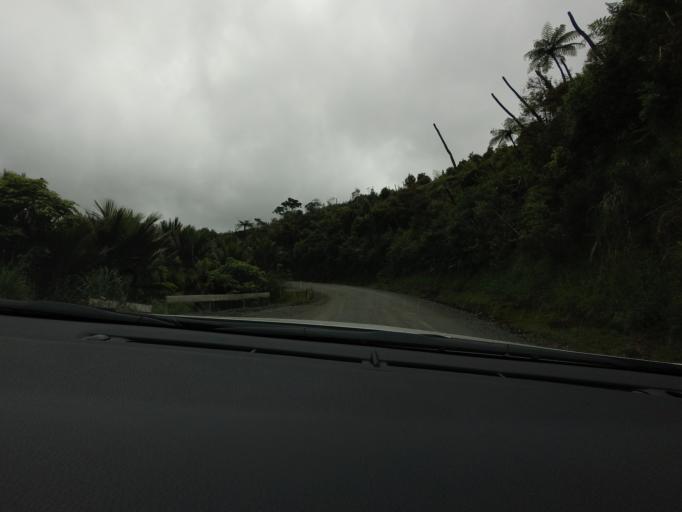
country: NZ
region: Auckland
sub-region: Auckland
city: Warkworth
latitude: -36.4837
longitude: 174.6056
